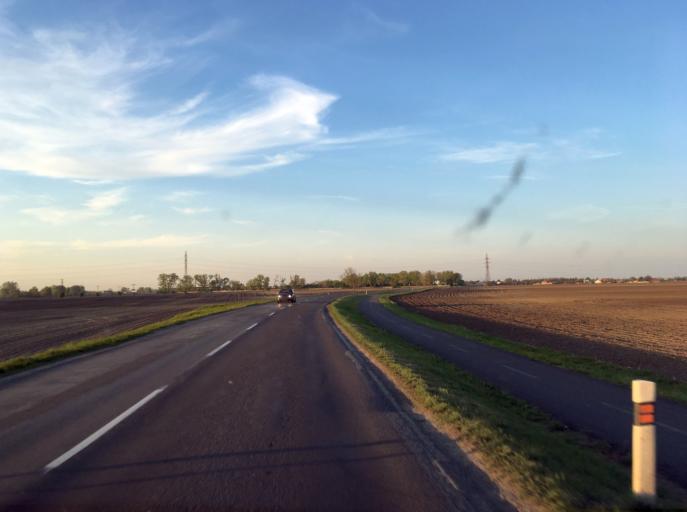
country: SK
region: Trnavsky
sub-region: Okres Dunajska Streda
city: Velky Meder
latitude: 47.8729
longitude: 17.7923
